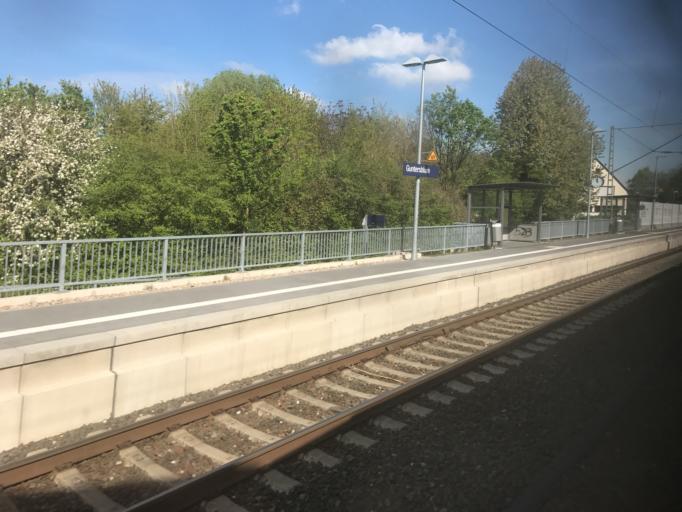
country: DE
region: Rheinland-Pfalz
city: Guntersblum
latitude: 49.7919
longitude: 8.3511
